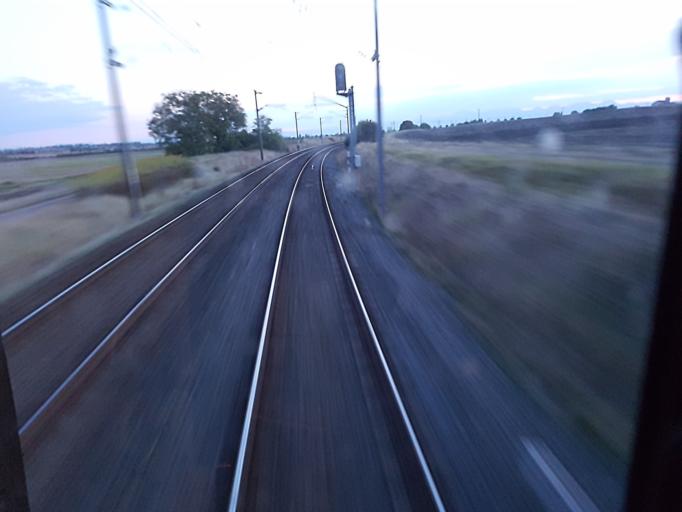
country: FR
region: Auvergne
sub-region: Departement du Puy-de-Dome
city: Randan
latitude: 45.9887
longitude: 3.3209
